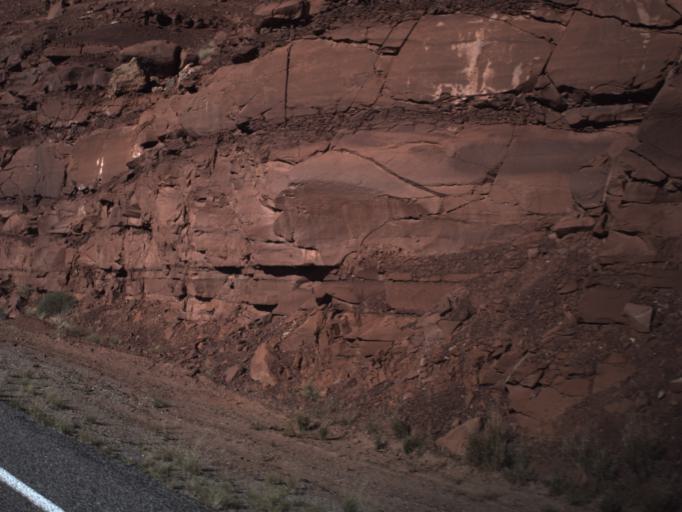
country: US
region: Utah
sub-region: San Juan County
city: Blanding
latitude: 37.8903
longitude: -110.4002
